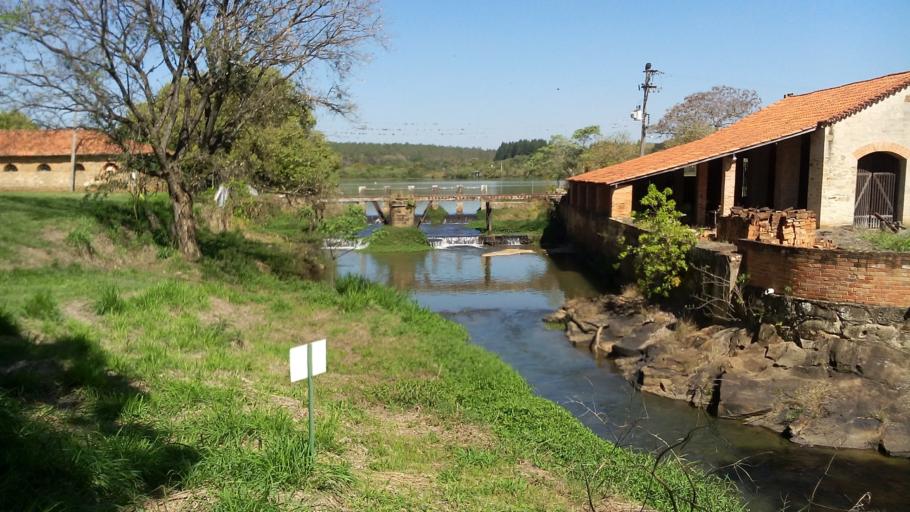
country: BR
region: Sao Paulo
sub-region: Aracoiaba Da Serra
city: Aracoiaba da Serra
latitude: -23.4251
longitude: -47.5957
